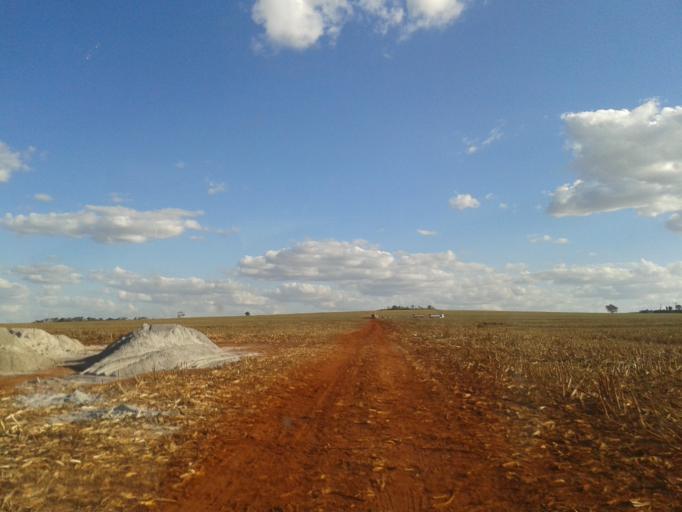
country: BR
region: Minas Gerais
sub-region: Centralina
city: Centralina
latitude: -18.6022
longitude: -49.2609
